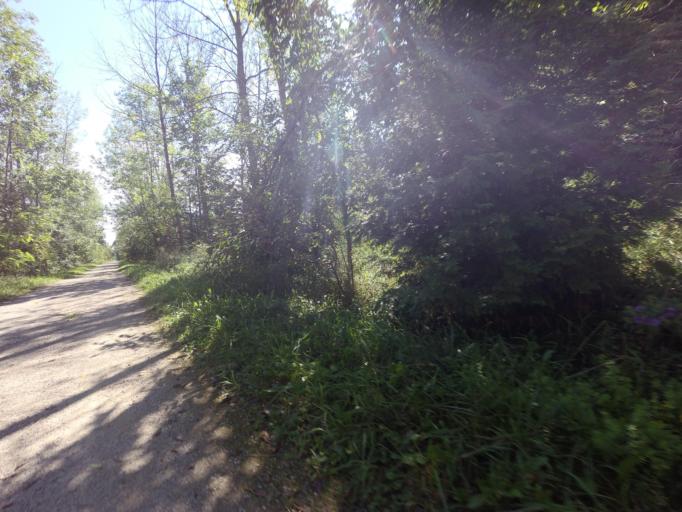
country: CA
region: Ontario
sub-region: Wellington County
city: Guelph
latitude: 43.6988
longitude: -80.3963
